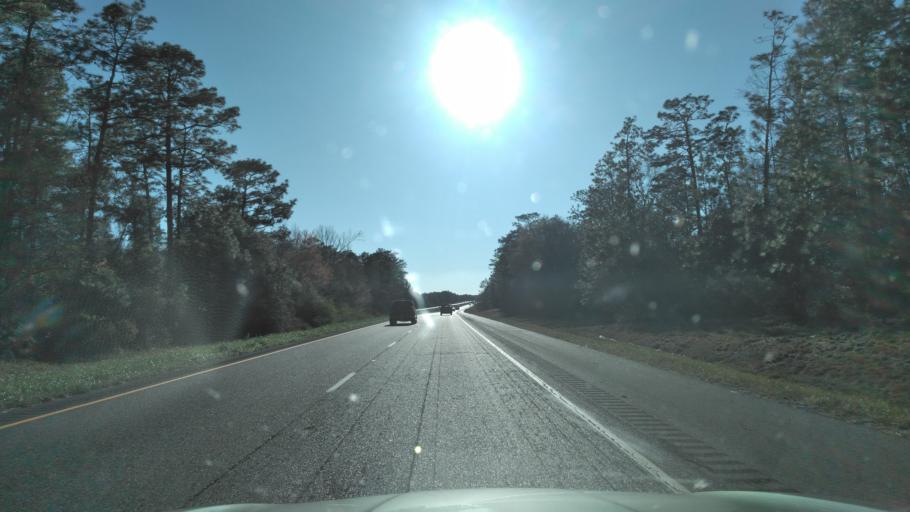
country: US
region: Alabama
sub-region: Escambia County
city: Atmore
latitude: 31.0439
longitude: -87.6083
